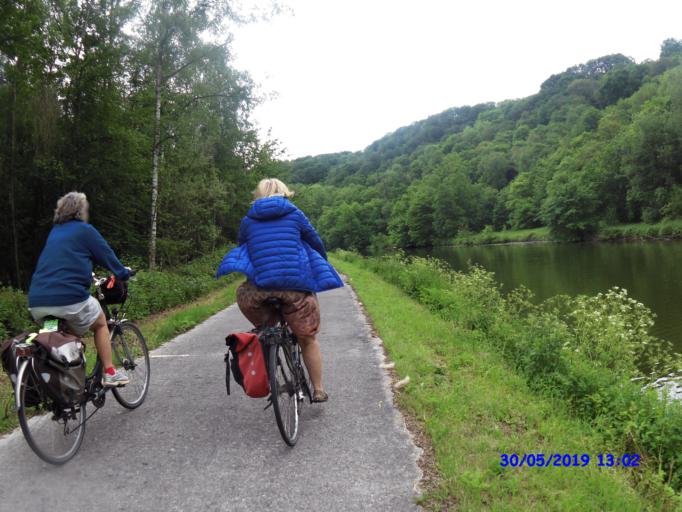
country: BE
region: Wallonia
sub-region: Province du Hainaut
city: Thuin
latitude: 50.3440
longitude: 4.3027
